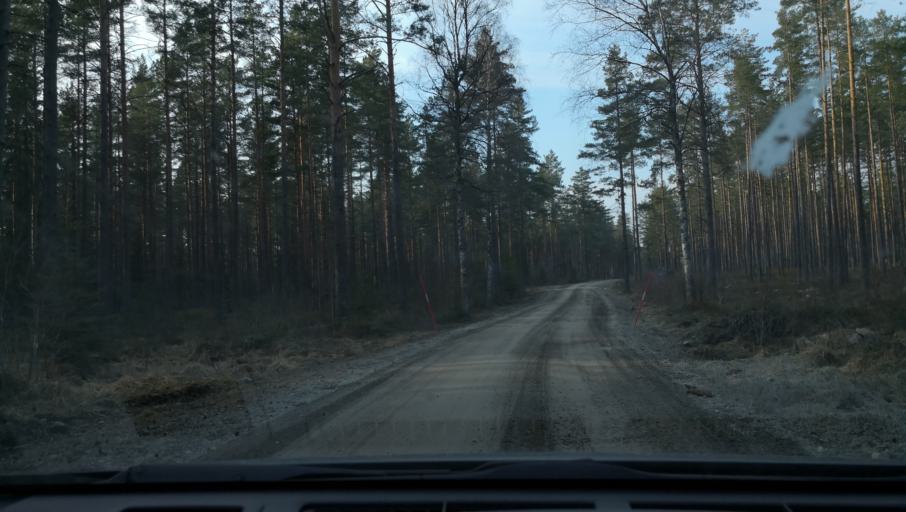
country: SE
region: OErebro
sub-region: Lindesbergs Kommun
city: Frovi
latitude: 59.3632
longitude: 15.3284
